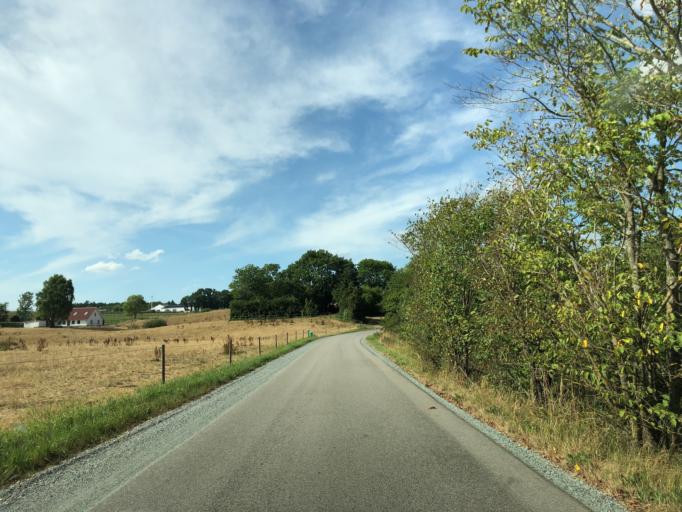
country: DK
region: South Denmark
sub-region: Vejle Kommune
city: Egtved
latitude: 55.6687
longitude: 9.3027
